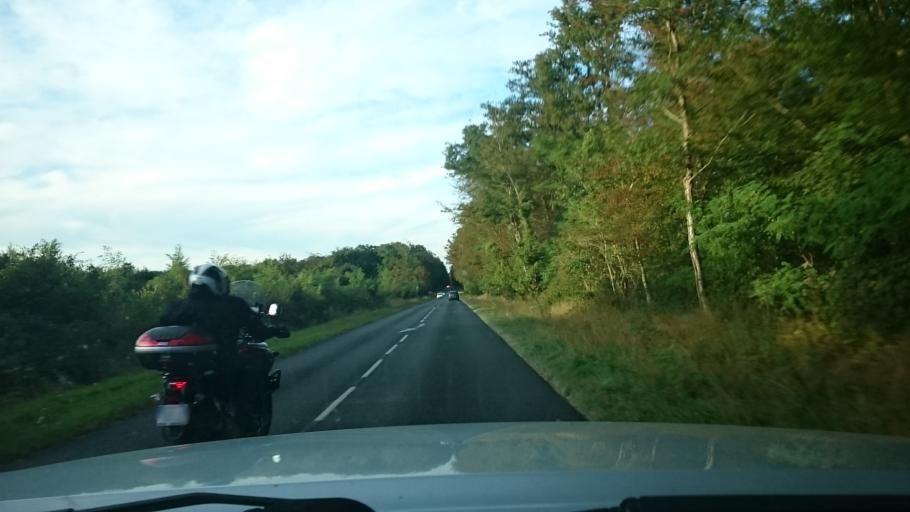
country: FR
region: Ile-de-France
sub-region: Departement de Seine-et-Marne
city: Samois-sur-Seine
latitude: 48.4688
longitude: 2.7391
